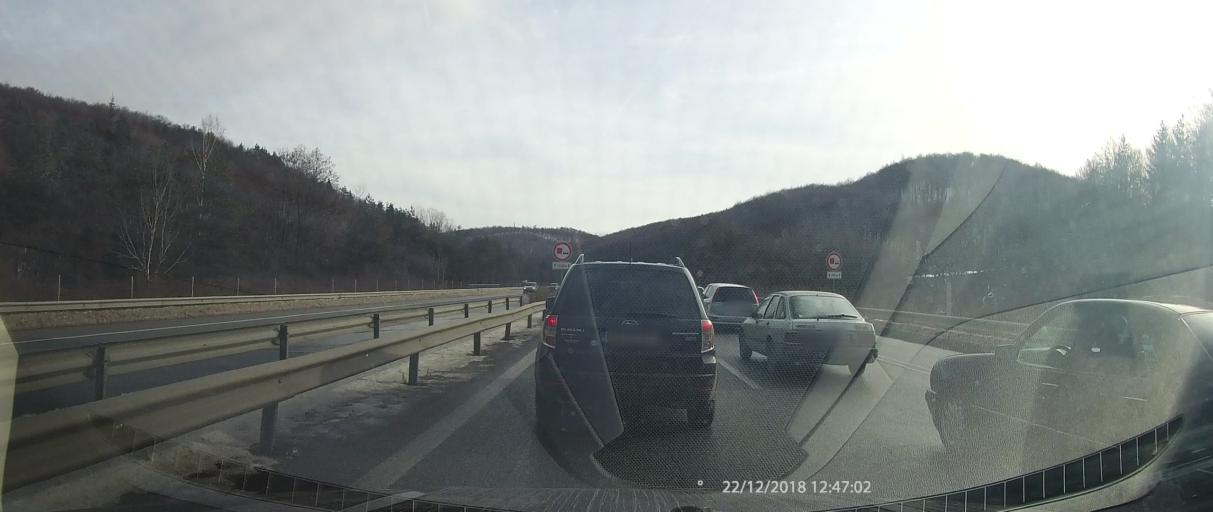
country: BG
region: Sofiya
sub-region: Obshtina Gorna Malina
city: Gorna Malina
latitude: 42.7769
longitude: 23.7748
